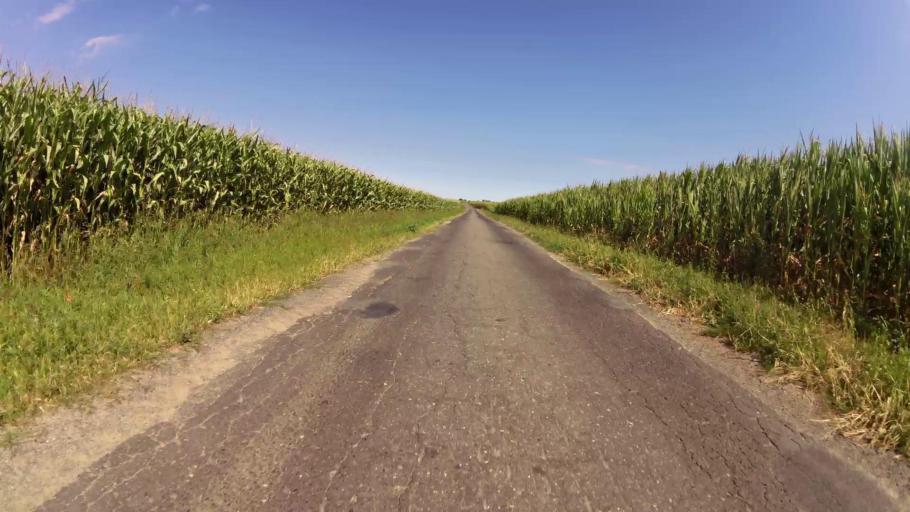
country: PL
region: West Pomeranian Voivodeship
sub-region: Powiat choszczenski
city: Choszczno
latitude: 53.2622
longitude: 15.4358
